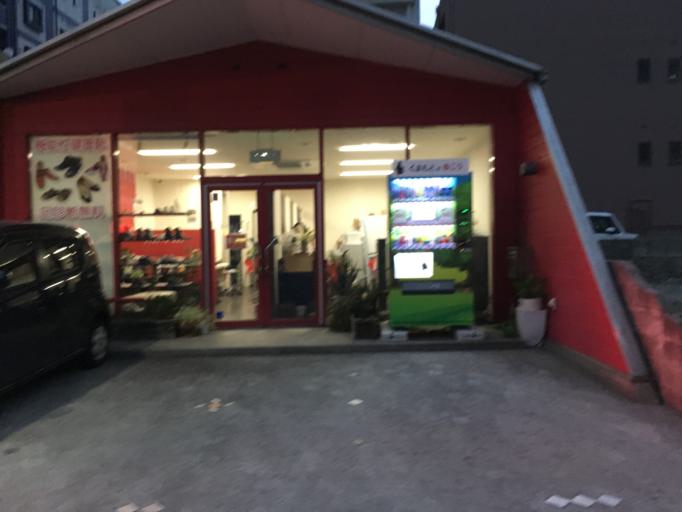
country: JP
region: Kumamoto
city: Kumamoto
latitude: 32.7942
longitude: 130.7263
